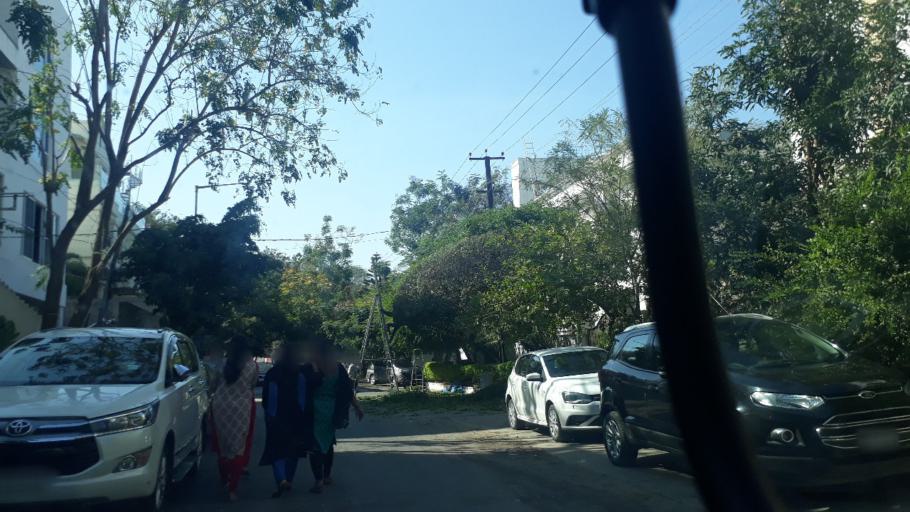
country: IN
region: Telangana
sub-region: Rangareddi
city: Kukatpalli
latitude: 17.4225
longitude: 78.4021
